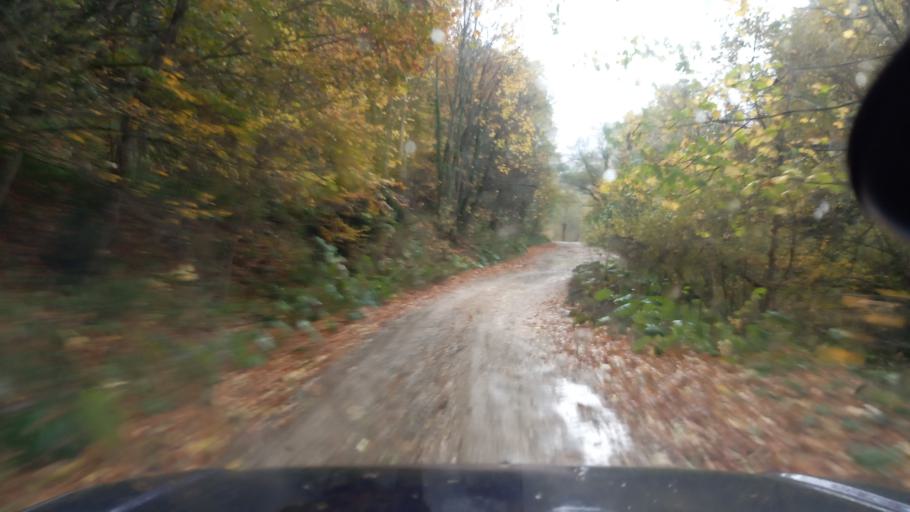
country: RU
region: Krasnodarskiy
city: Neftegorsk
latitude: 44.0360
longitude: 39.8358
